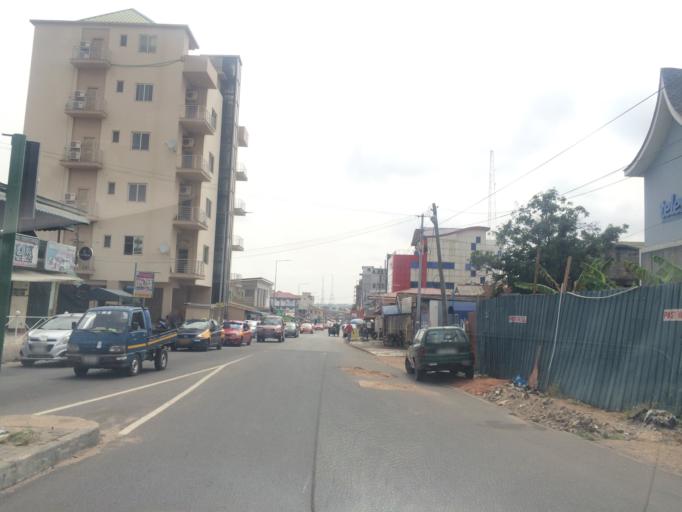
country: GH
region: Greater Accra
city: Accra
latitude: 5.5658
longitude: -0.2118
